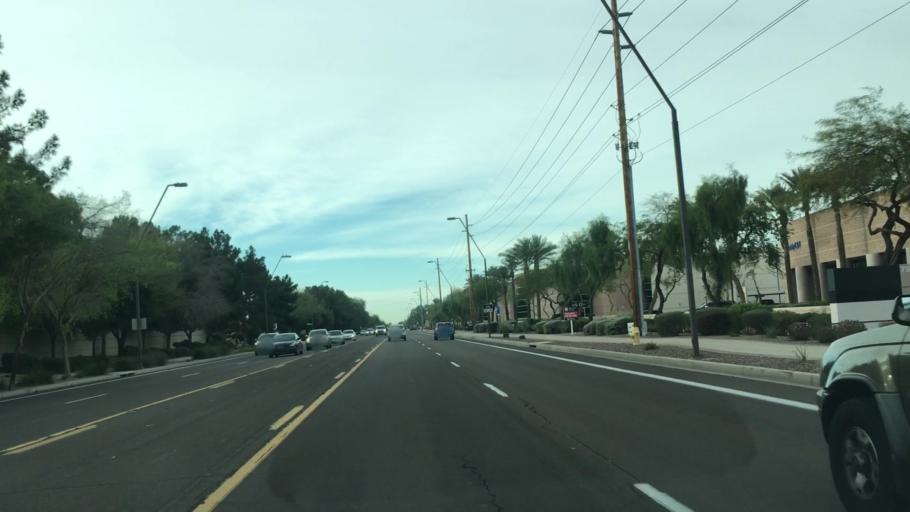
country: US
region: Arizona
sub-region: Maricopa County
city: Guadalupe
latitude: 33.3458
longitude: -111.9458
